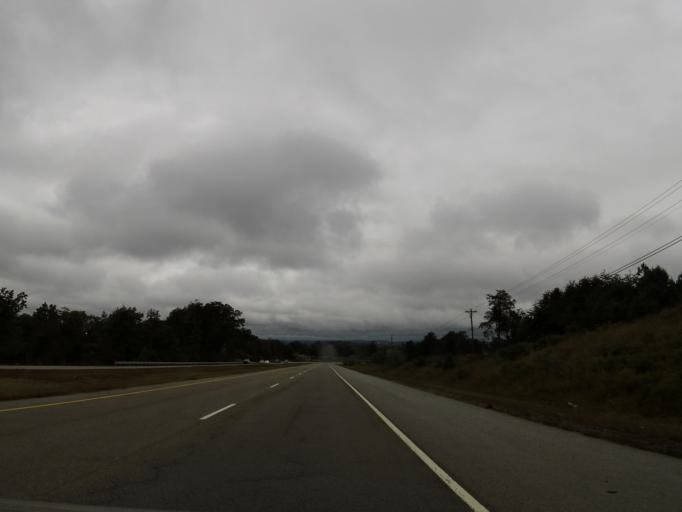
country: US
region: Tennessee
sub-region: Loudon County
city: Lenoir City
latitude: 35.7581
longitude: -84.2211
